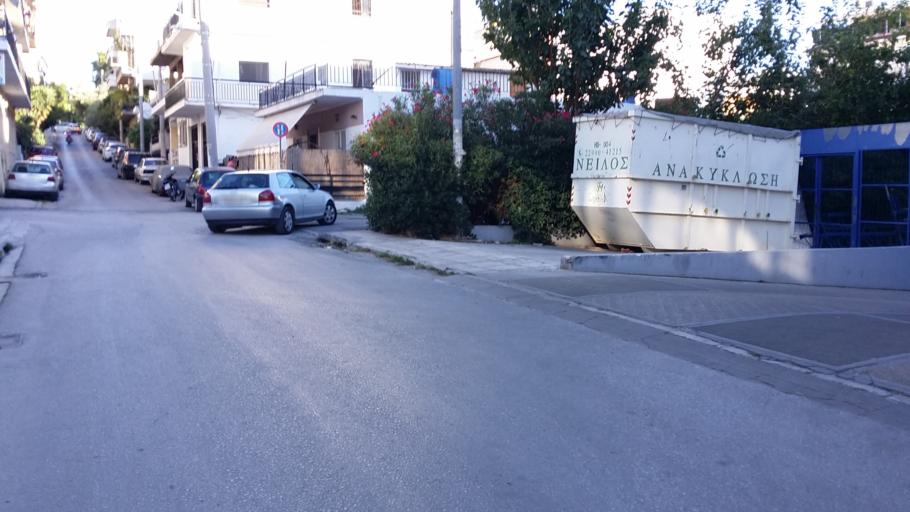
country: GR
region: Attica
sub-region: Nomarchia Athinas
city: Irakleio
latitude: 38.0533
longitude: 23.7533
